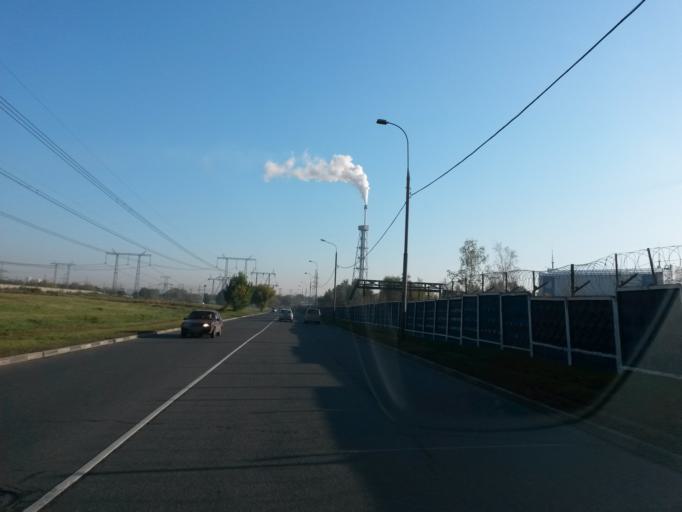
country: RU
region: Moscow
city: Kapotnya
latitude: 55.6533
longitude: 37.7923
